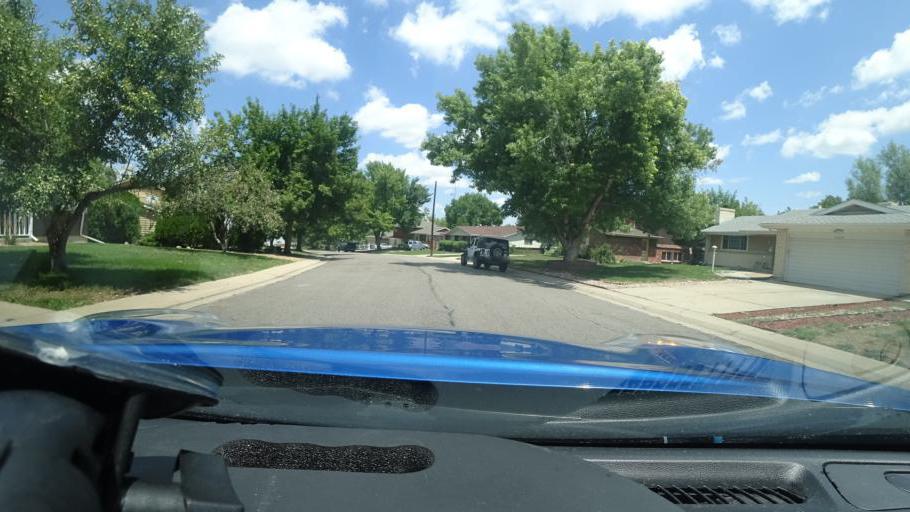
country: US
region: Colorado
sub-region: Adams County
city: Aurora
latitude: 39.7093
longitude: -104.8391
